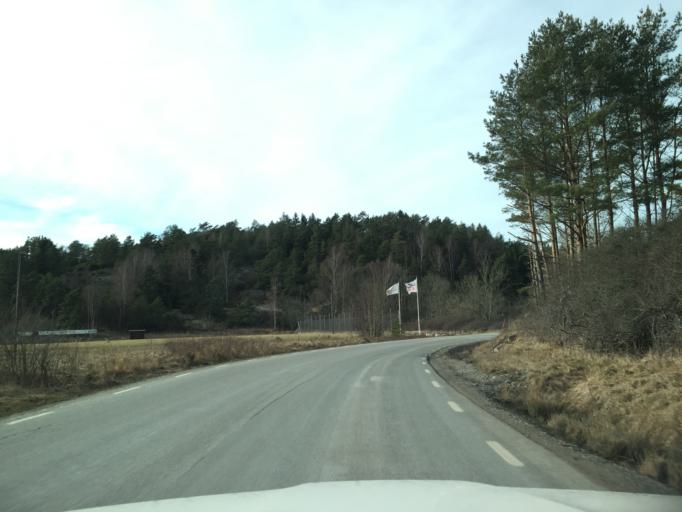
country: SE
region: Vaestra Goetaland
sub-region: Tjorns Kommun
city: Skaerhamn
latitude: 58.0306
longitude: 11.5963
